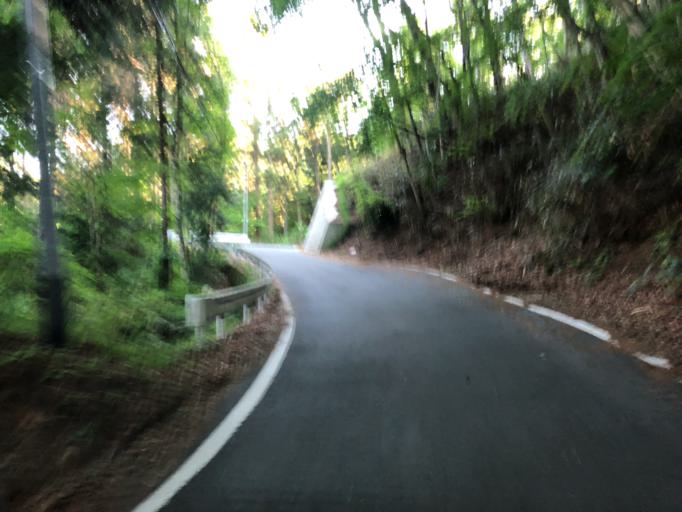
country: JP
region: Ibaraki
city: Kitaibaraki
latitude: 36.8978
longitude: 140.6153
